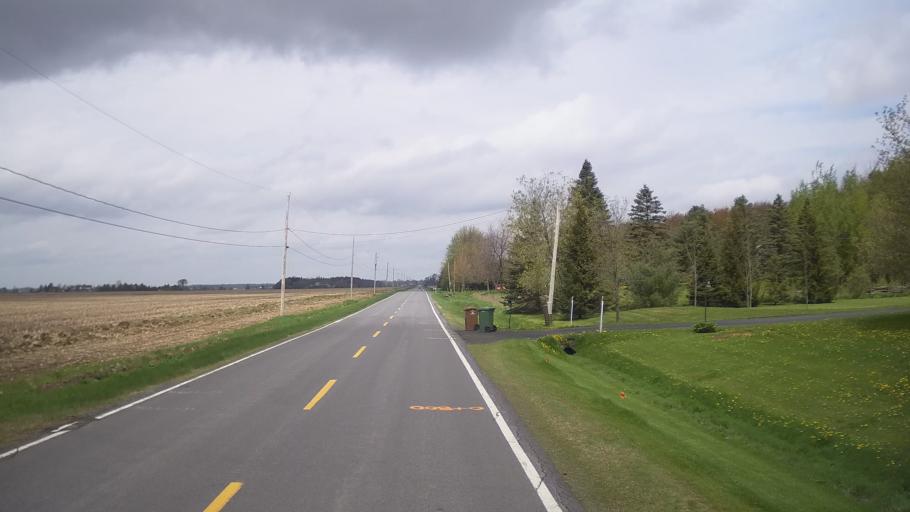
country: CA
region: Quebec
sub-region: Monteregie
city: Marieville
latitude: 45.3155
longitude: -73.1291
